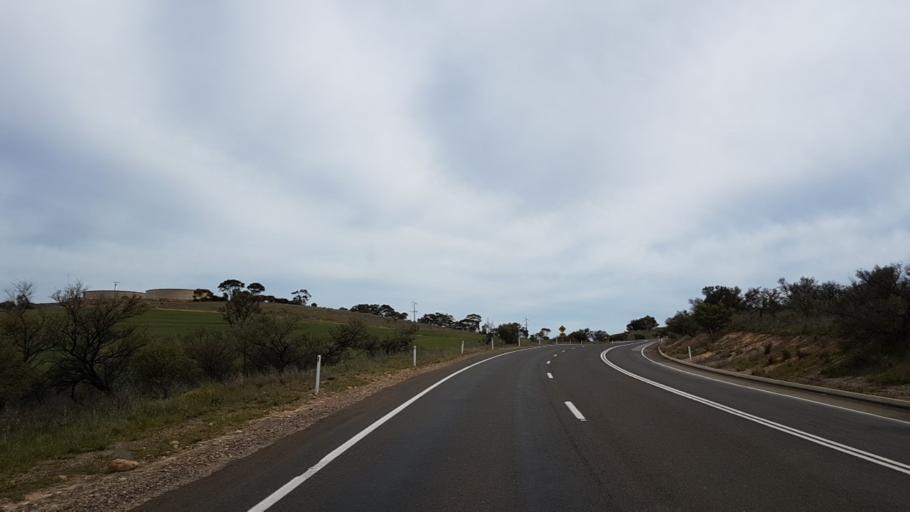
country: AU
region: South Australia
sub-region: Port Pirie City and Dists
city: Crystal Brook
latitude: -33.2855
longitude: 138.2341
